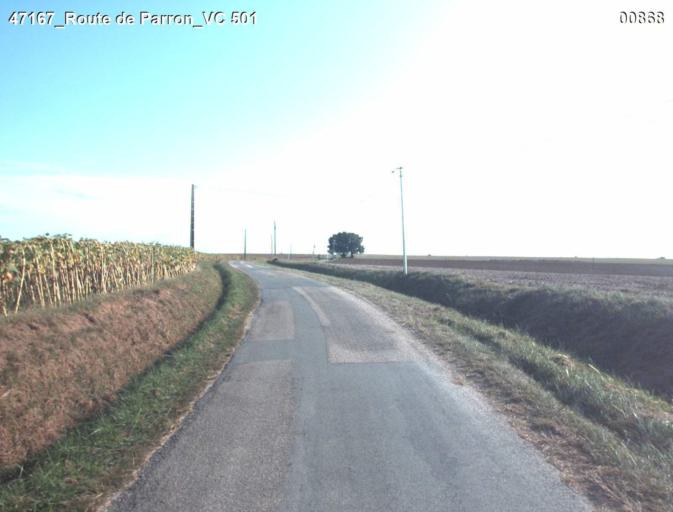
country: FR
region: Aquitaine
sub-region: Departement du Lot-et-Garonne
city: Mezin
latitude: 44.0444
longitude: 0.2698
